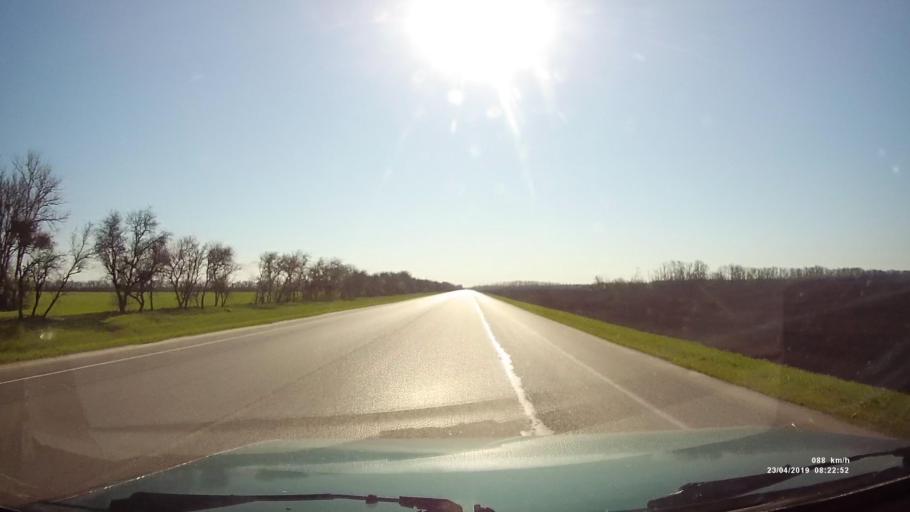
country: RU
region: Rostov
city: Tselina
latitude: 46.5343
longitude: 40.9180
